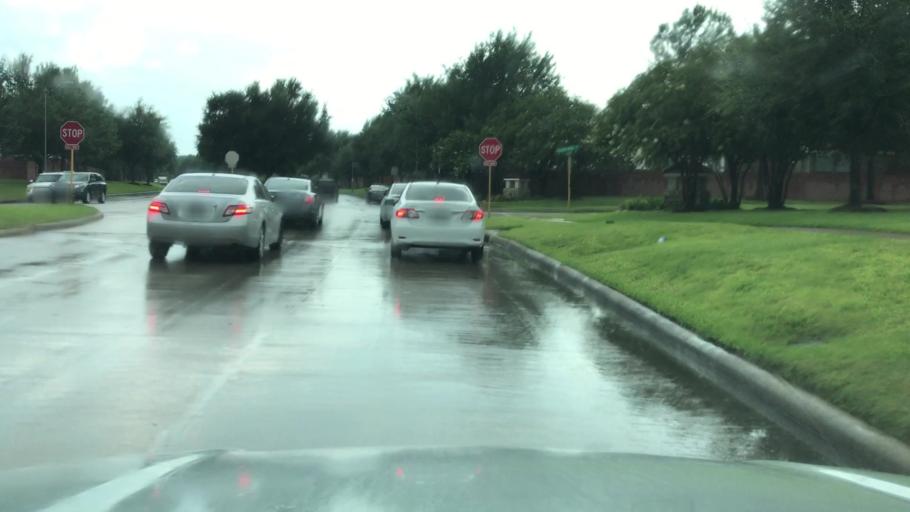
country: US
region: Texas
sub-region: Fort Bend County
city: Cinco Ranch
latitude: 29.7494
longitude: -95.7869
